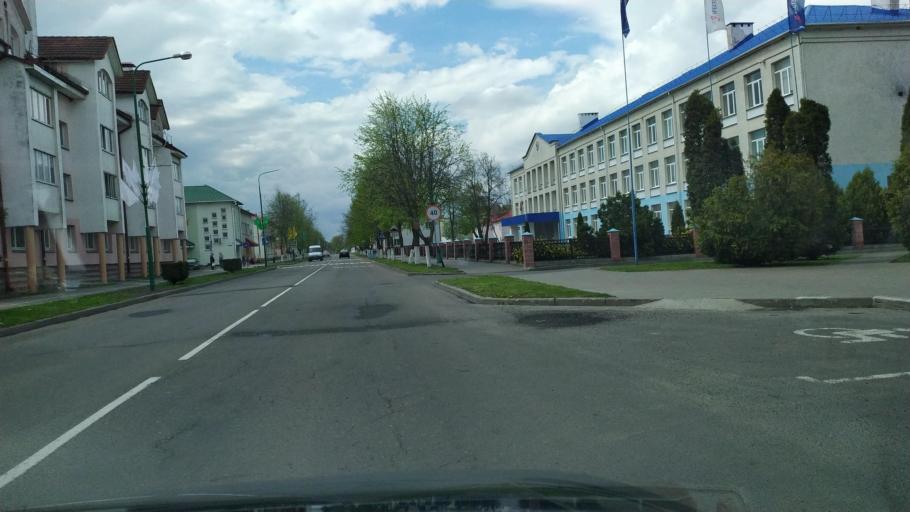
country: BY
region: Brest
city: Pruzhany
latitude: 52.5550
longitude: 24.4608
